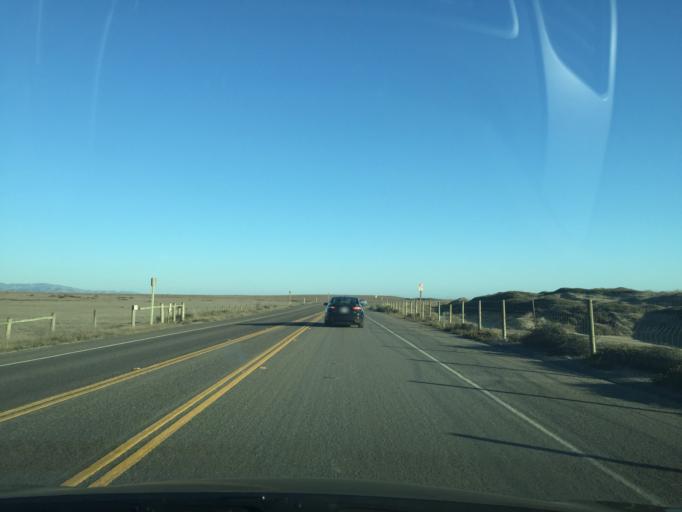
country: US
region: California
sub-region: San Luis Obispo County
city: Cambria
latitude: 35.6616
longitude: -121.2545
